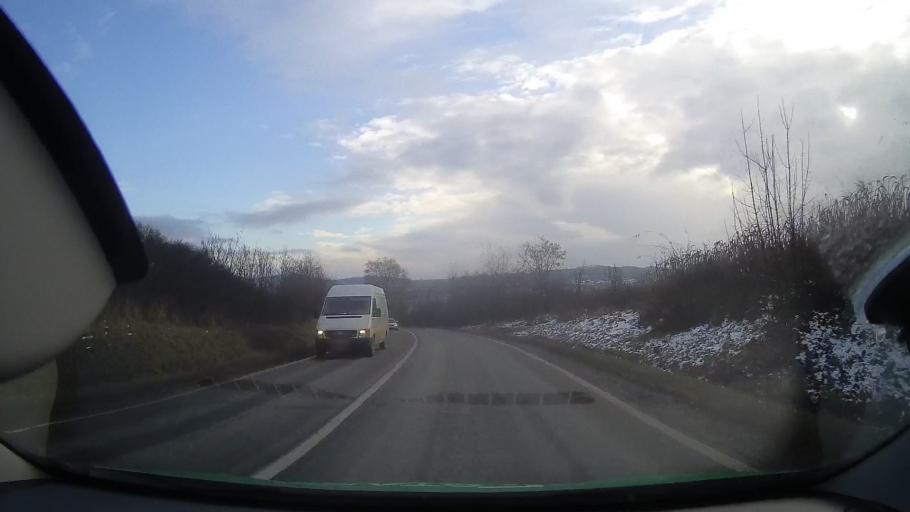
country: RO
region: Mures
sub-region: Comuna Cucerdea
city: Cucerdea
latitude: 46.4114
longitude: 24.2649
